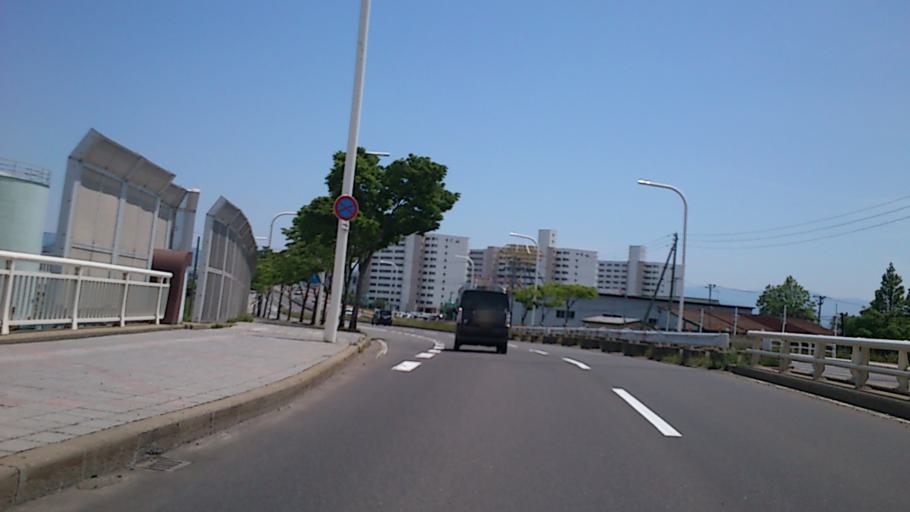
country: JP
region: Aomori
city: Aomori Shi
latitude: 40.8340
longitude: 140.7278
